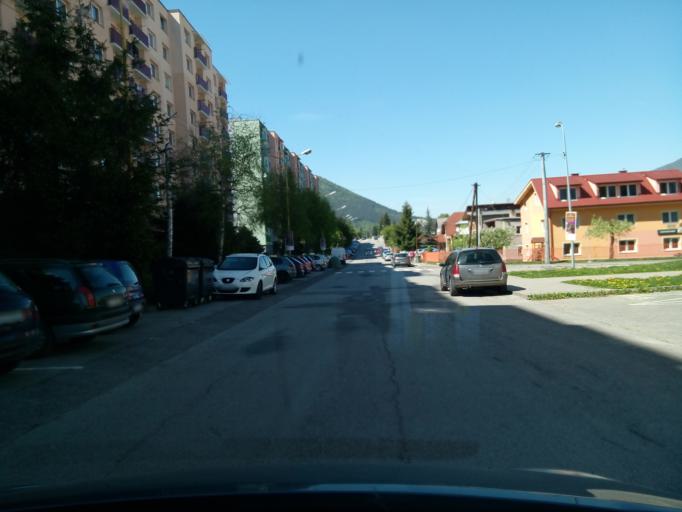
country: SK
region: Zilinsky
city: Ruzomberok
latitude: 49.0649
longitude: 19.3000
